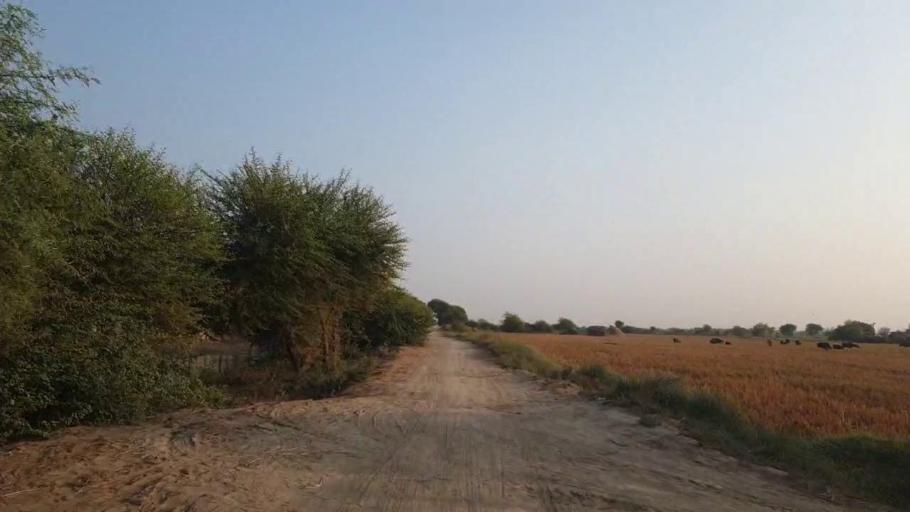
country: PK
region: Sindh
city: Kario
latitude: 24.8572
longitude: 68.6269
